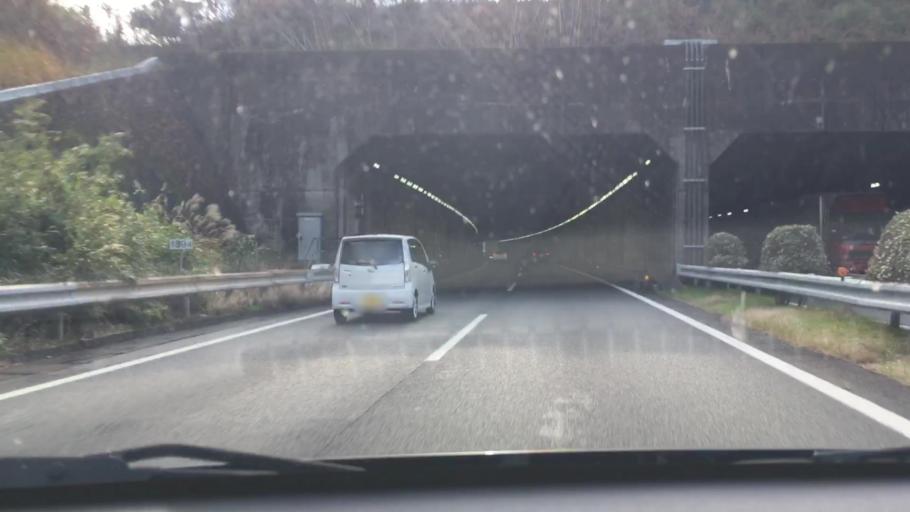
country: JP
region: Kumamoto
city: Uto
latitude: 32.6909
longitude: 130.7382
